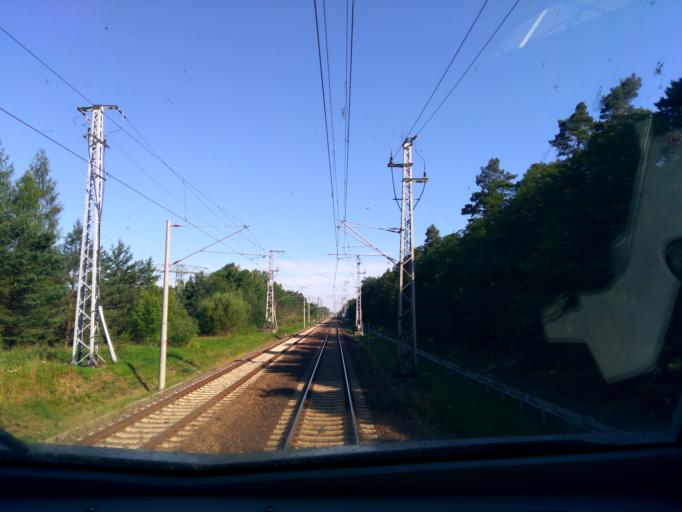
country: DE
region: Brandenburg
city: Halbe
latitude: 52.1166
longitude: 13.6932
